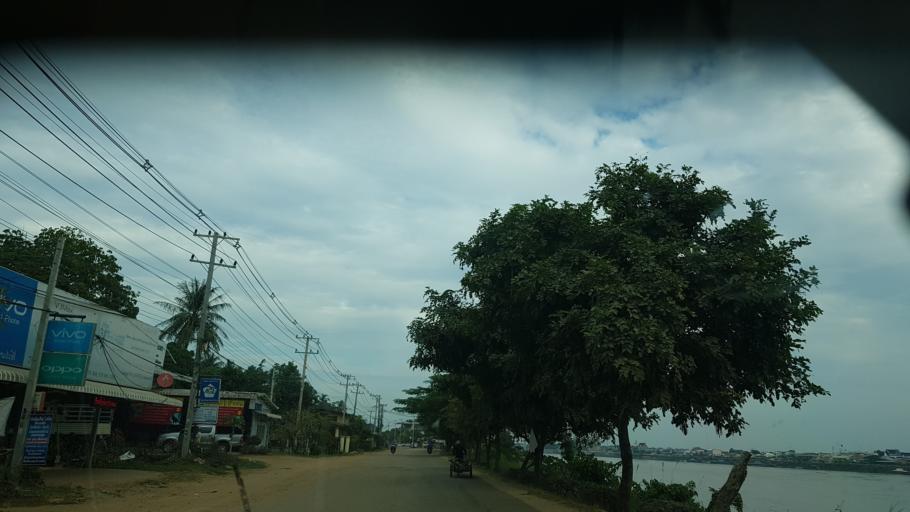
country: TH
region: Nong Khai
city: Nong Khai
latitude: 17.8885
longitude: 102.7365
